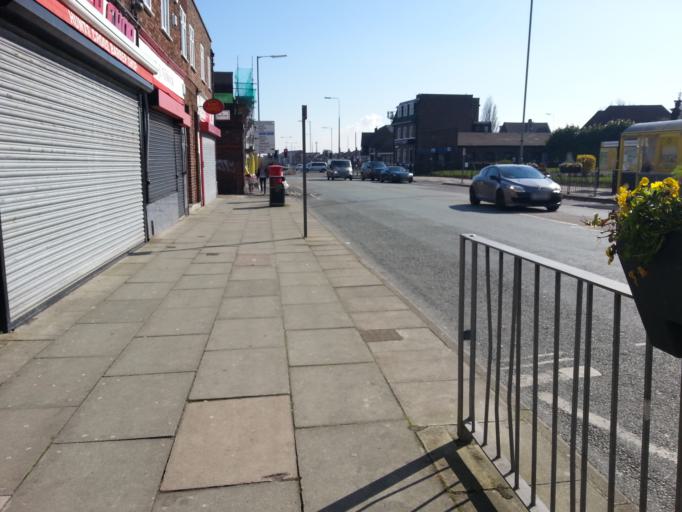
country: GB
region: England
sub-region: Knowsley
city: Huyton
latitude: 53.3601
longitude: -2.8562
